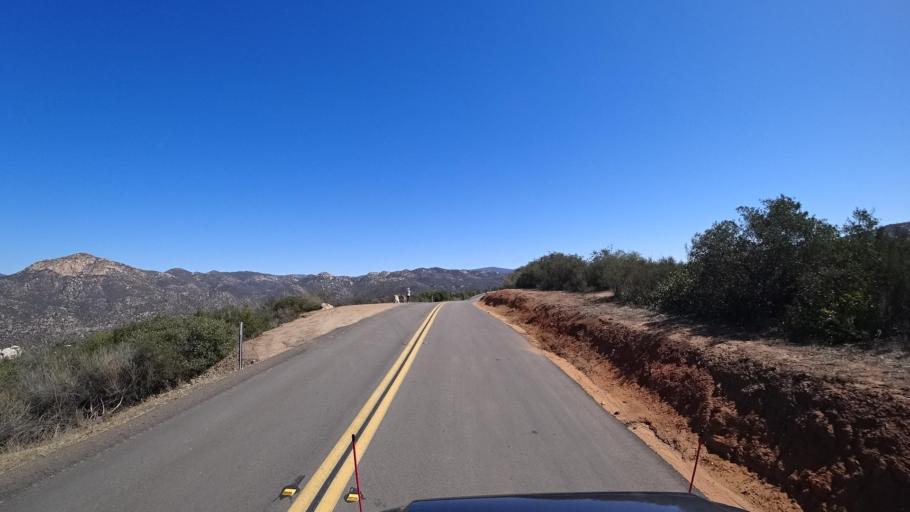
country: US
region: California
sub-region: San Diego County
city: Alpine
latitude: 32.7778
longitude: -116.7231
